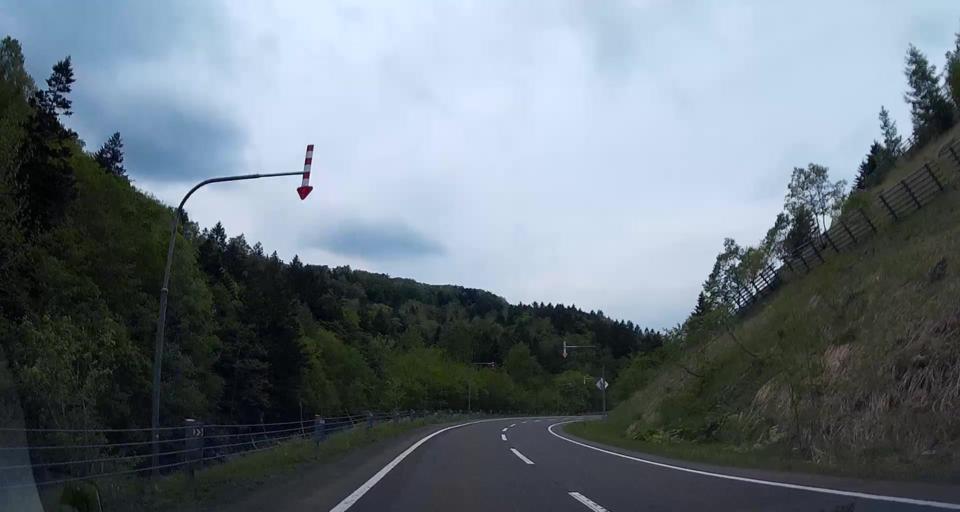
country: JP
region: Hokkaido
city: Shiraoi
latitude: 42.6771
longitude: 141.1223
